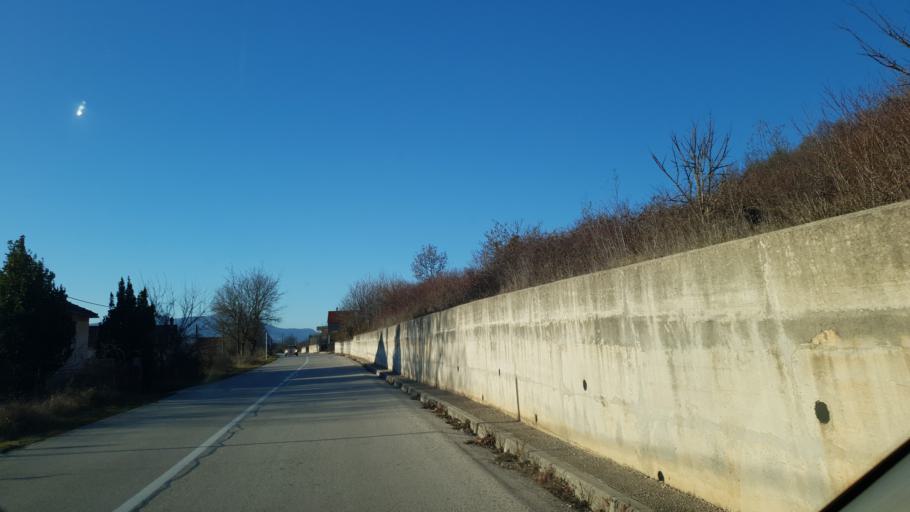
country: HR
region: Splitsko-Dalmatinska
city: Gala
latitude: 43.7323
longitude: 16.6906
